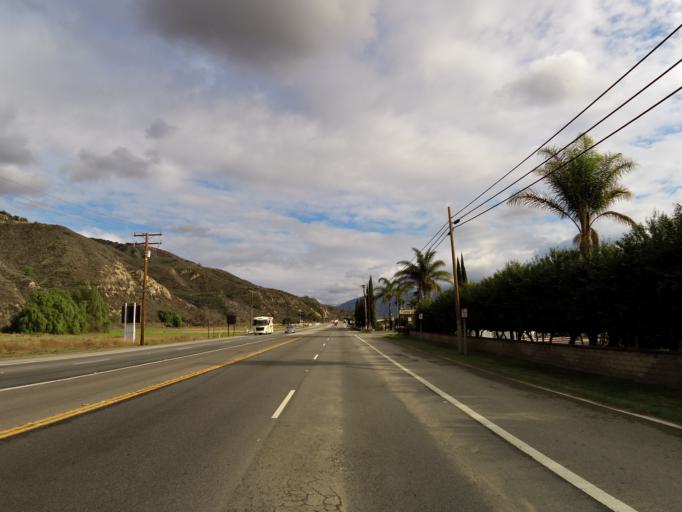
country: US
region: California
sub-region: Ventura County
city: Fillmore
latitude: 34.3987
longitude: -118.8996
